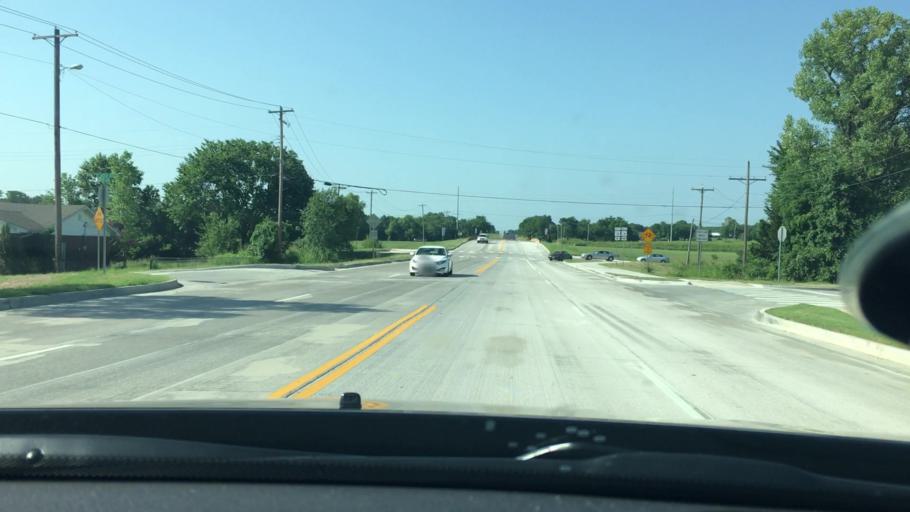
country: US
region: Oklahoma
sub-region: Pontotoc County
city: Ada
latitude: 34.7545
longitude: -96.6701
